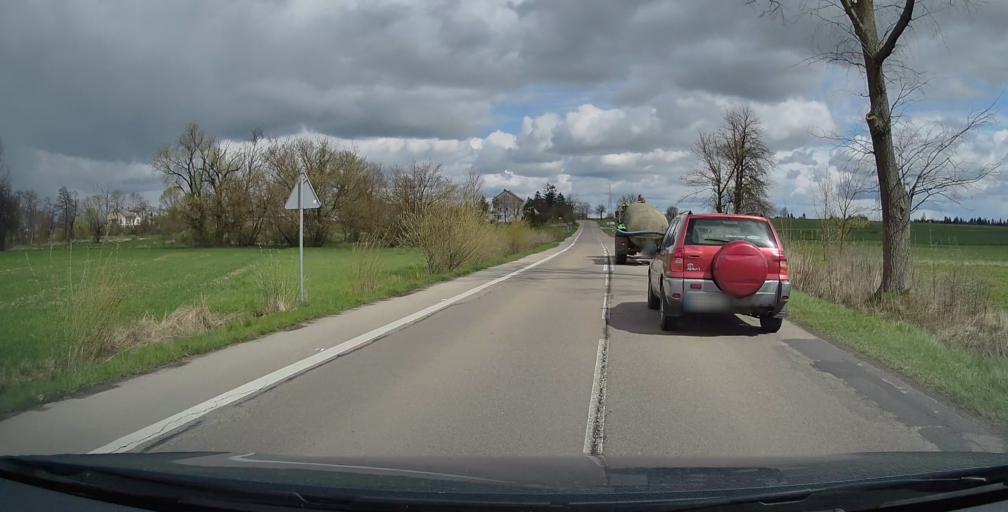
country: PL
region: Masovian Voivodeship
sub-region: Powiat ostrolecki
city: Goworowo
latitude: 52.8743
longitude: 21.5659
